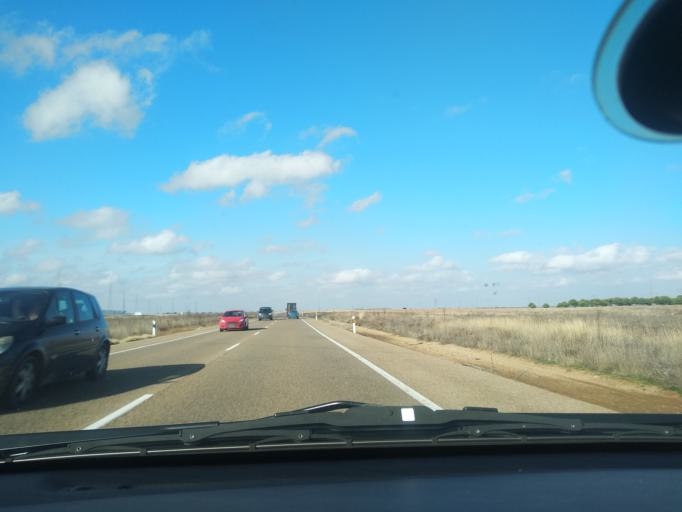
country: ES
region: Castille and Leon
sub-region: Provincia de Valladolid
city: Valdenebro de los Valles
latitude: 41.7930
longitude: -4.9543
